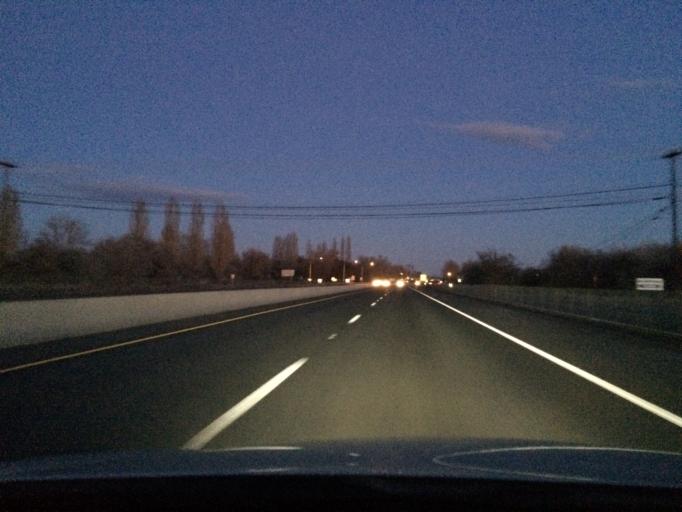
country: US
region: Washington
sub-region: Grant County
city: Cascade Valley
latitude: 47.1039
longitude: -119.3356
